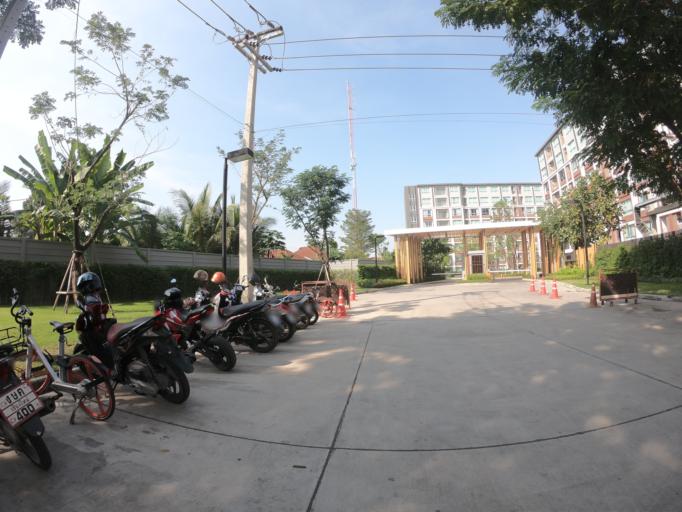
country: TH
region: Chiang Mai
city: Chiang Mai
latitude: 18.8101
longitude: 99.0156
